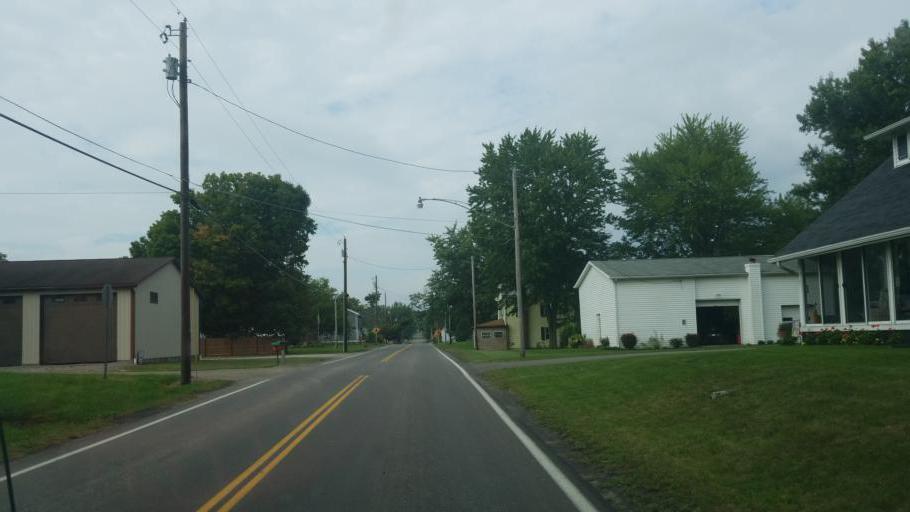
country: US
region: Ohio
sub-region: Wayne County
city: West Salem
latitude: 40.9227
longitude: -82.0521
